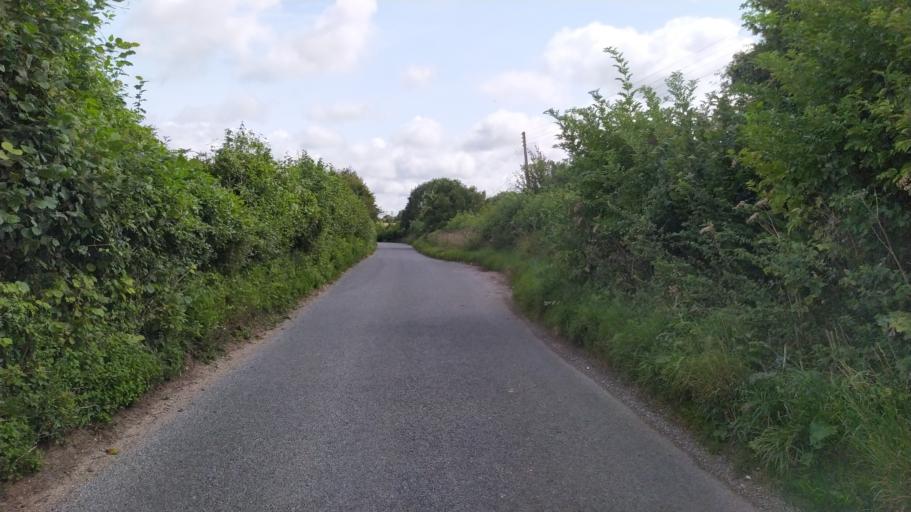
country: GB
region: England
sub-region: Dorset
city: Blandford Forum
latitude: 50.8396
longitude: -2.1302
